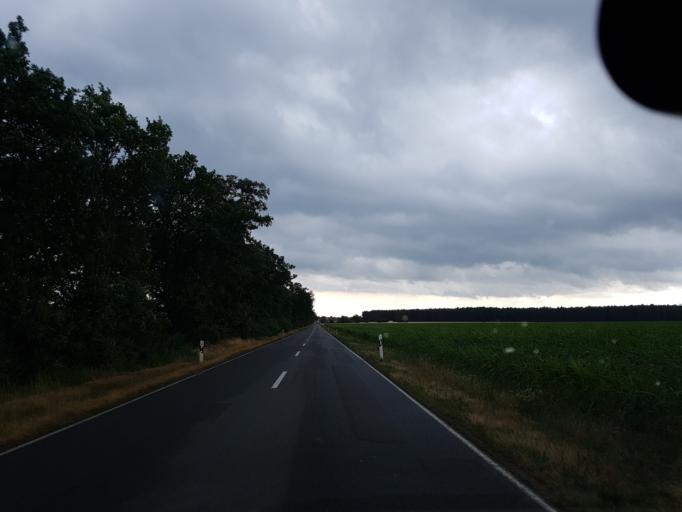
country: DE
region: Saxony-Anhalt
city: Seyda
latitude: 51.9135
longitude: 12.9450
